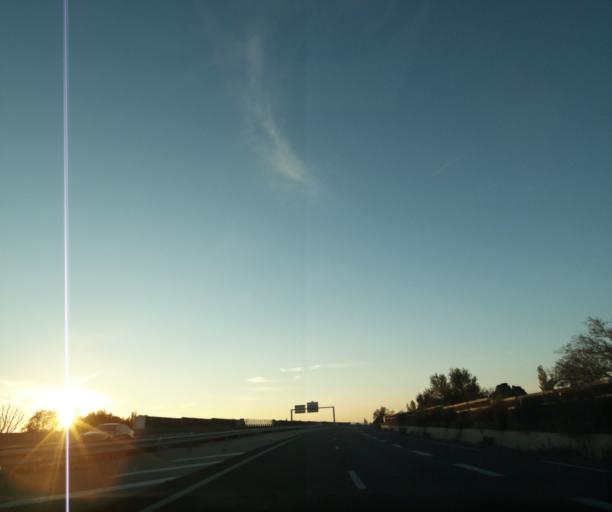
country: FR
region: Provence-Alpes-Cote d'Azur
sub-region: Departement des Bouches-du-Rhone
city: Grans
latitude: 43.6246
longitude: 5.0776
